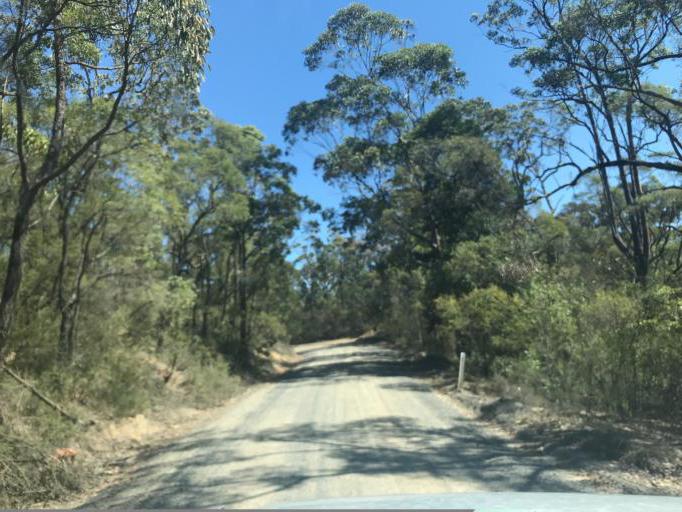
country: AU
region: New South Wales
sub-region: Wyong Shire
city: Little Jilliby
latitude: -33.1483
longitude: 151.0805
